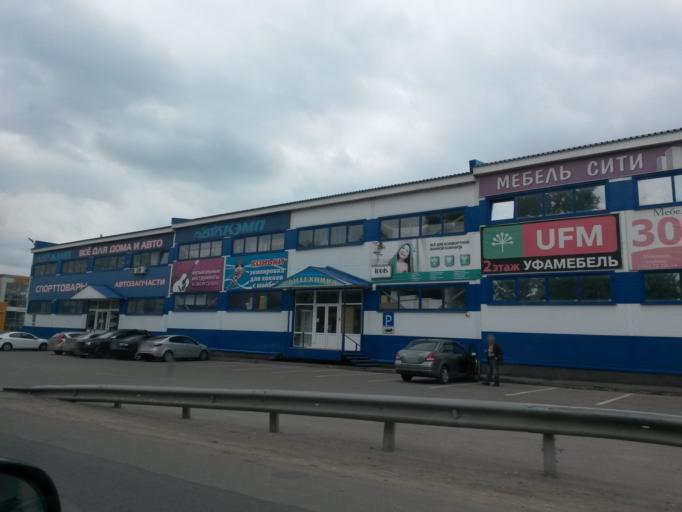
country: RU
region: Moskovskaya
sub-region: Chekhovskiy Rayon
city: Chekhov
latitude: 55.1637
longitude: 37.4669
